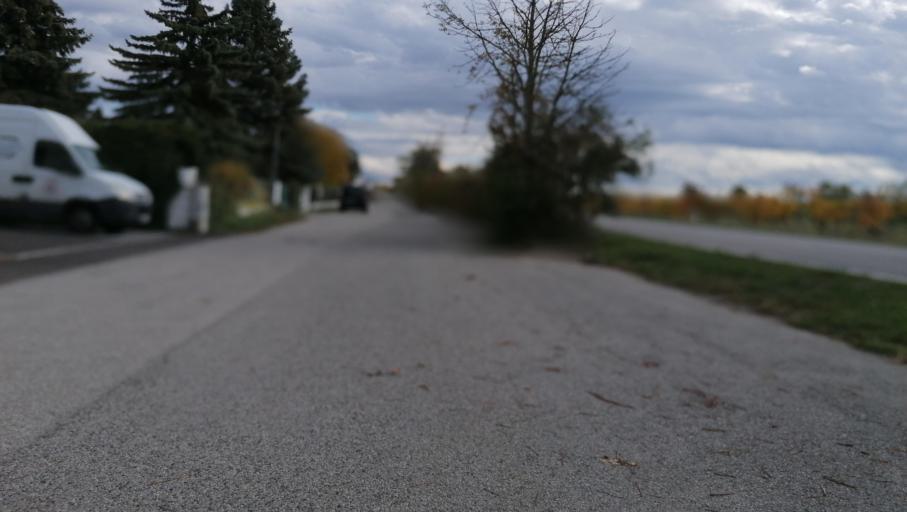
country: AT
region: Lower Austria
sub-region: Politischer Bezirk Baden
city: Tattendorf
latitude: 47.9505
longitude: 16.3093
